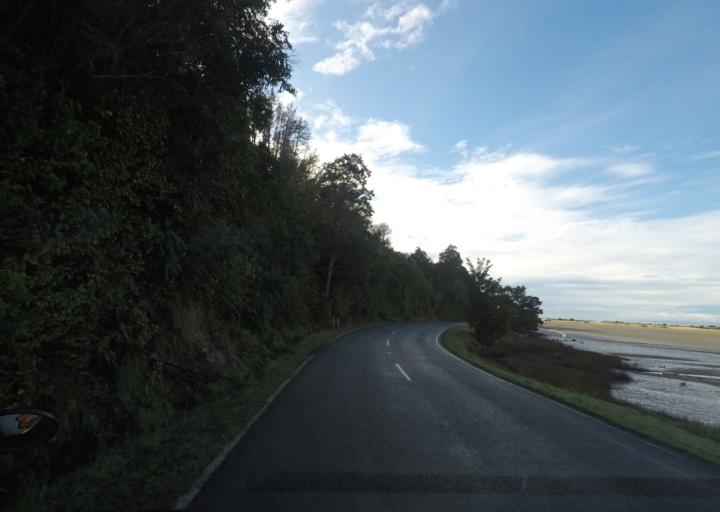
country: NZ
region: Tasman
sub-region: Tasman District
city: Motueka
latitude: -41.0121
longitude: 173.0002
